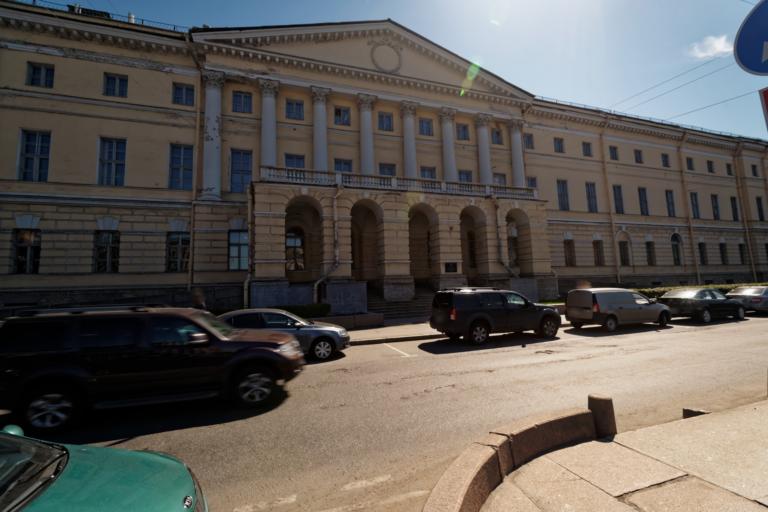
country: RU
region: St.-Petersburg
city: Centralniy
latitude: 59.9351
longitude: 30.3447
